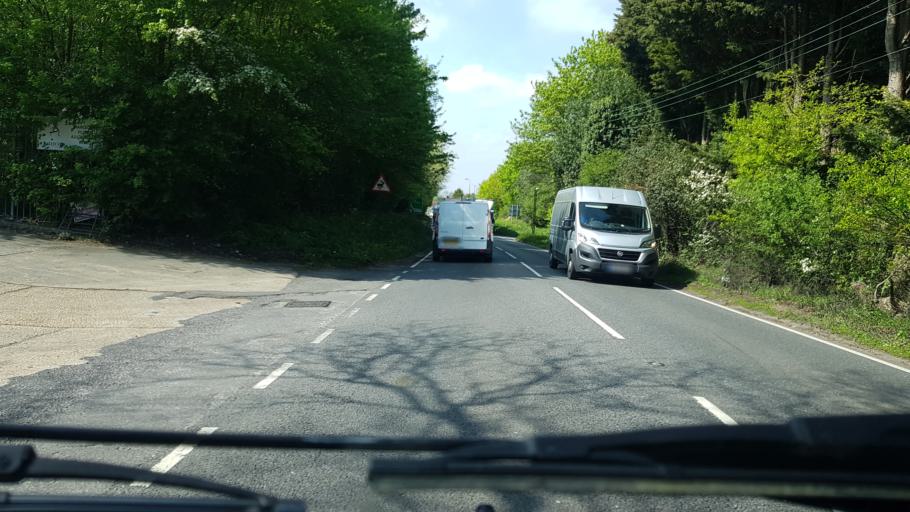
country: GB
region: England
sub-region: Kent
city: Pembury
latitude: 51.1325
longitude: 0.3551
